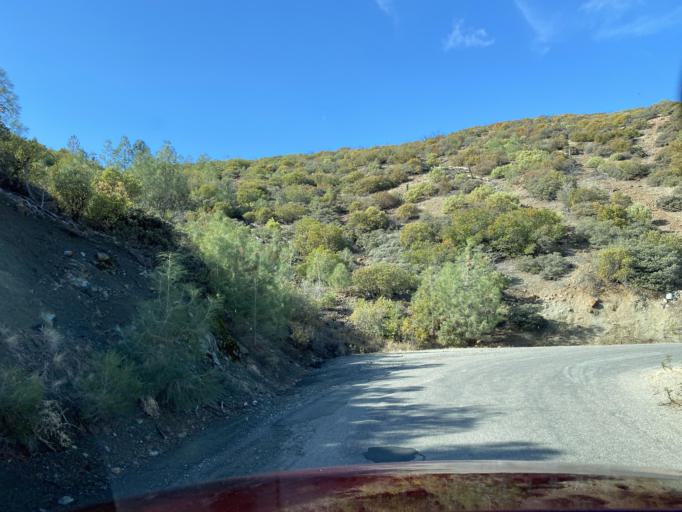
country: US
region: California
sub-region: Lake County
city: Lucerne
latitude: 39.3661
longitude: -122.6354
